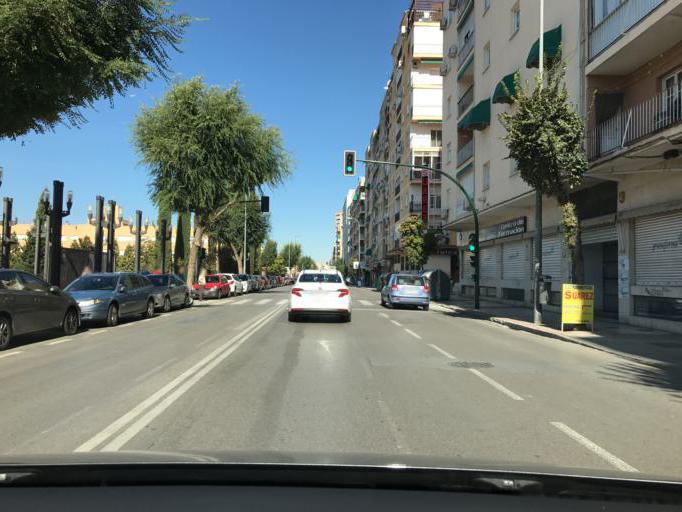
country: ES
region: Andalusia
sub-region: Provincia de Granada
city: Granada
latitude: 37.1716
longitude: -3.6083
